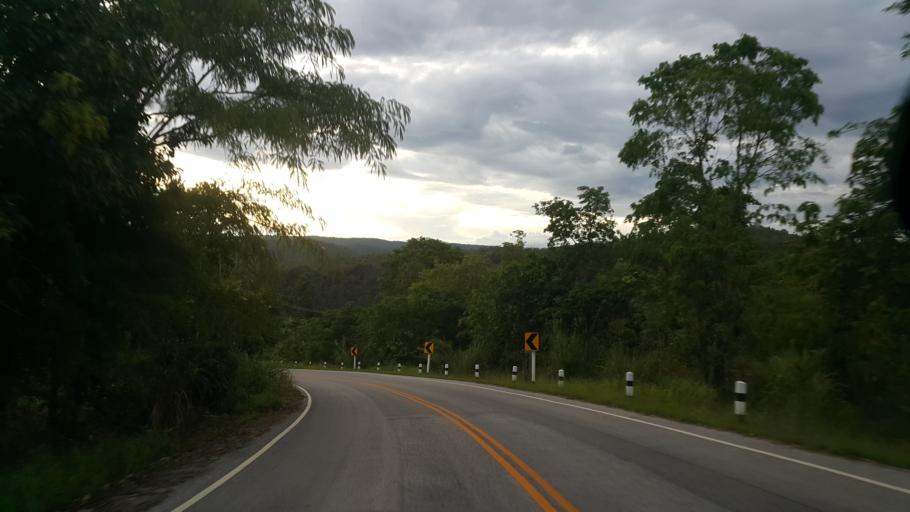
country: TH
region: Loei
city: Na Haeo
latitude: 17.4904
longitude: 101.1755
